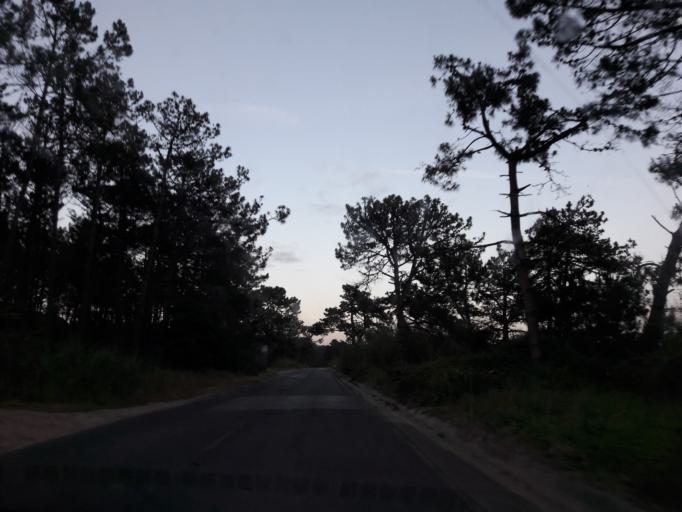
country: PT
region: Leiria
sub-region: Peniche
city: Atouguia da Baleia
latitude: 39.3585
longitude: -9.3012
